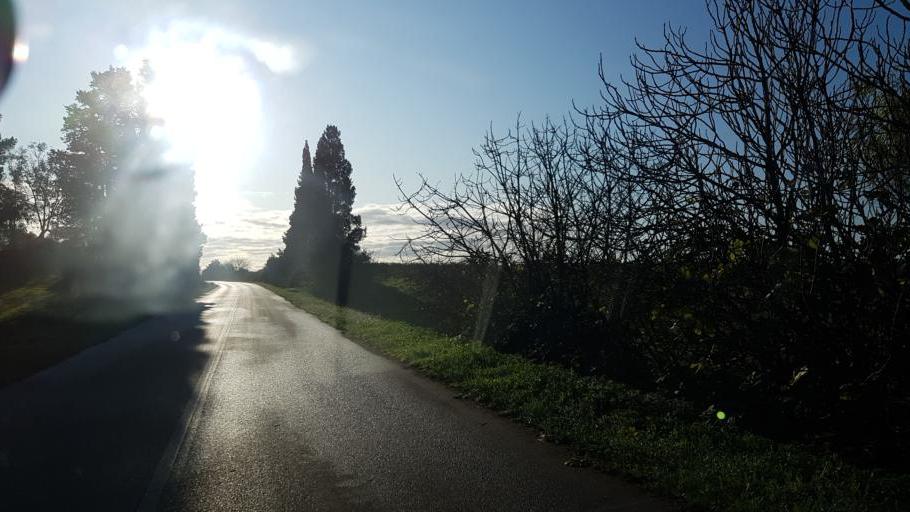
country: IT
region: Apulia
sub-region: Provincia di Brindisi
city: Torchiarolo
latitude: 40.5467
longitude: 18.0435
